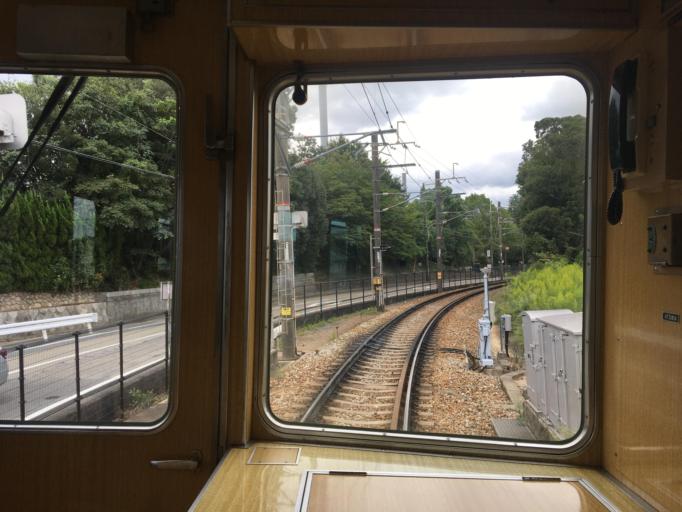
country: JP
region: Hyogo
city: Nishinomiya-hama
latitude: 34.7573
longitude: 135.3325
